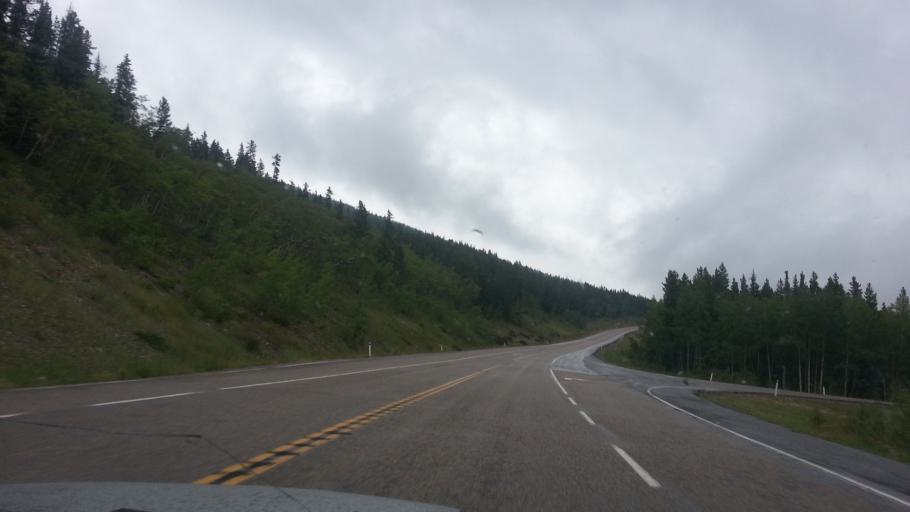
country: CA
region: Alberta
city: Cochrane
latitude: 50.8677
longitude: -114.7856
